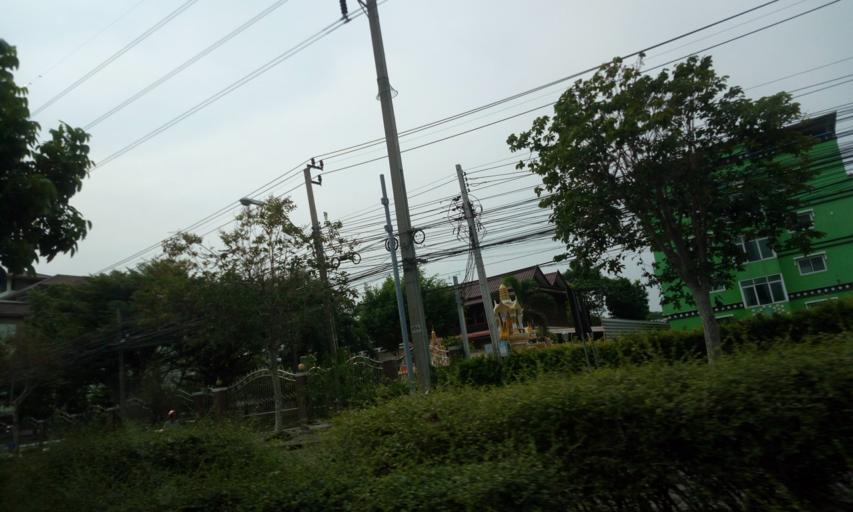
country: TH
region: Bangkok
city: Lat Krabang
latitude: 13.7217
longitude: 100.7693
